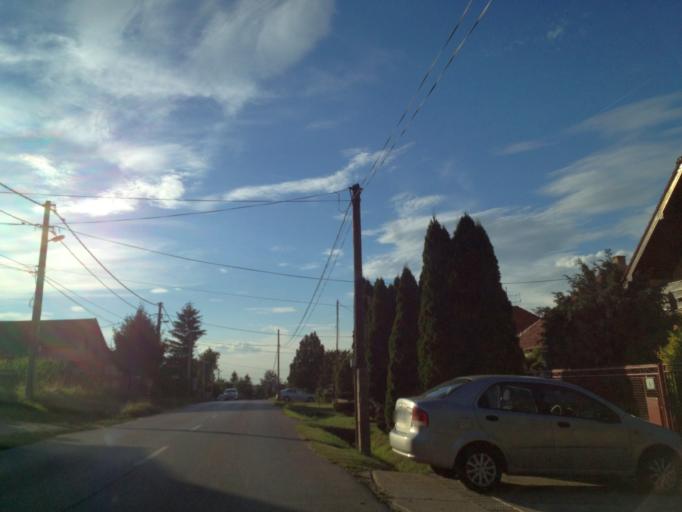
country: SK
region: Nitriansky
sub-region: Okres Komarno
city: Hurbanovo
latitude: 47.8647
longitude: 18.2697
